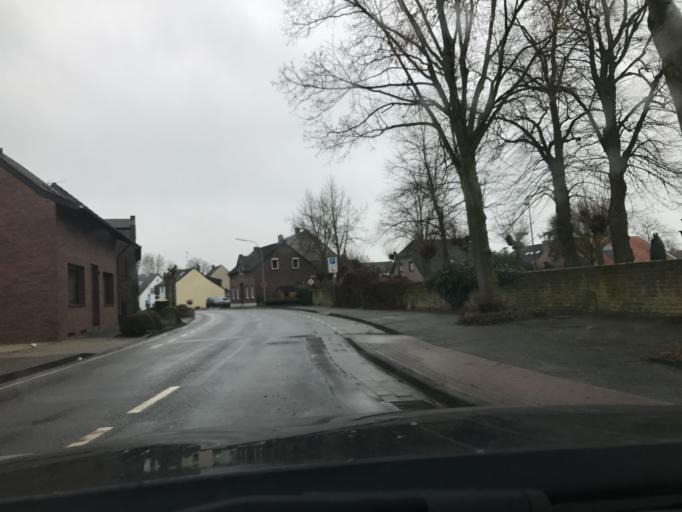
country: DE
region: North Rhine-Westphalia
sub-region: Regierungsbezirk Dusseldorf
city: Wachtendonk
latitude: 51.4107
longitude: 6.3353
